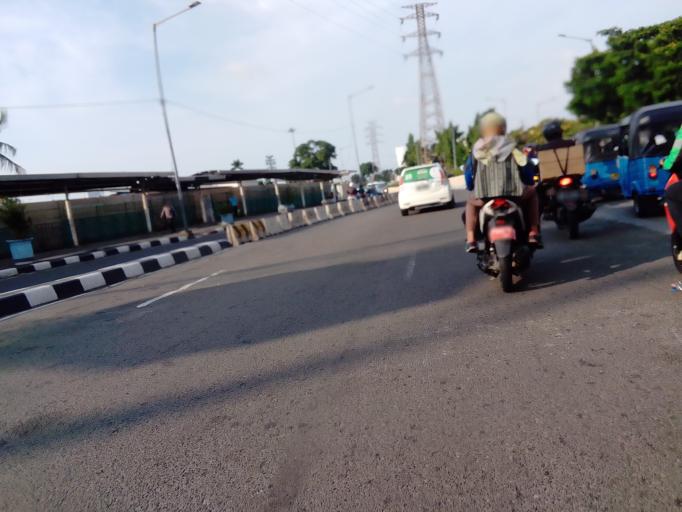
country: ID
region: Jakarta Raya
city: Jakarta
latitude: -6.1780
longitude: 106.8426
